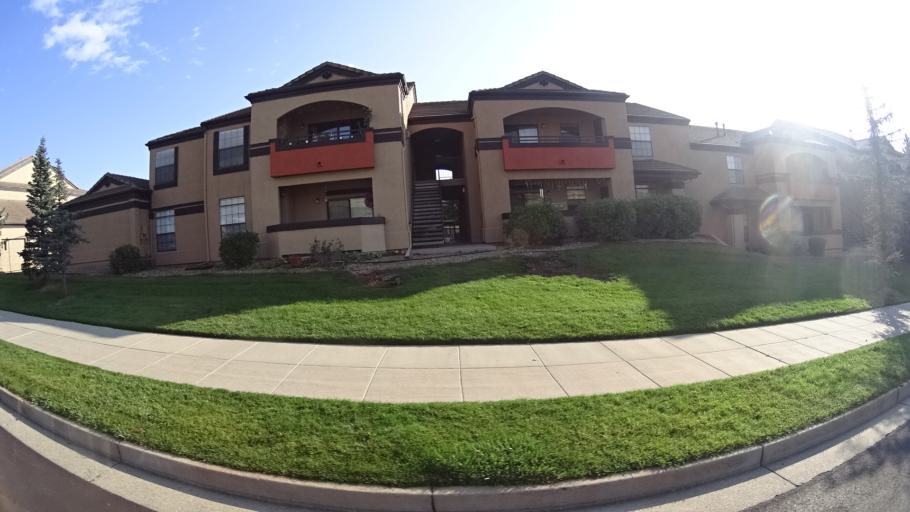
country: US
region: Colorado
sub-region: El Paso County
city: Manitou Springs
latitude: 38.8973
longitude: -104.8713
